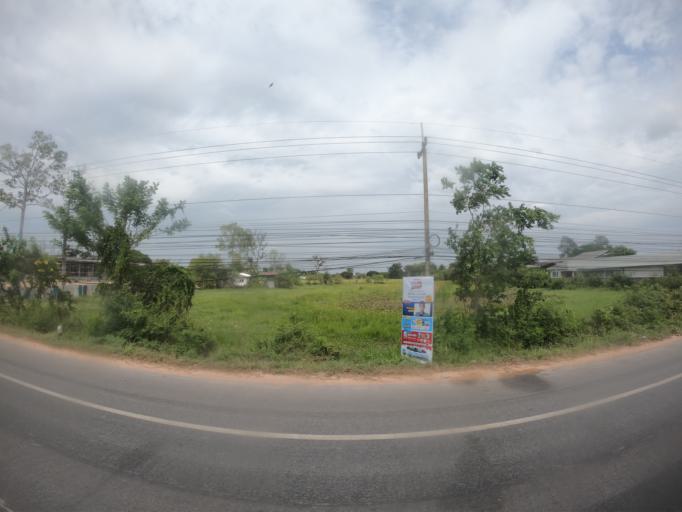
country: TH
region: Roi Et
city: Roi Et
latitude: 16.0660
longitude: 103.6132
